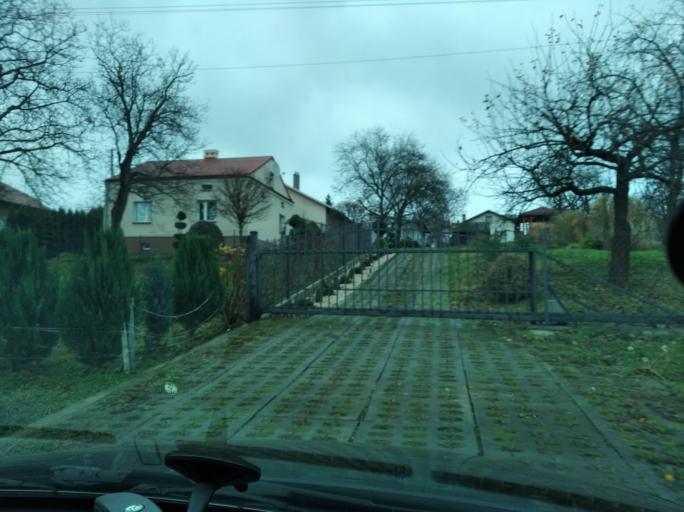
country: PL
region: Subcarpathian Voivodeship
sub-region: Powiat przeworski
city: Sietesz
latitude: 49.9989
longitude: 22.3555
